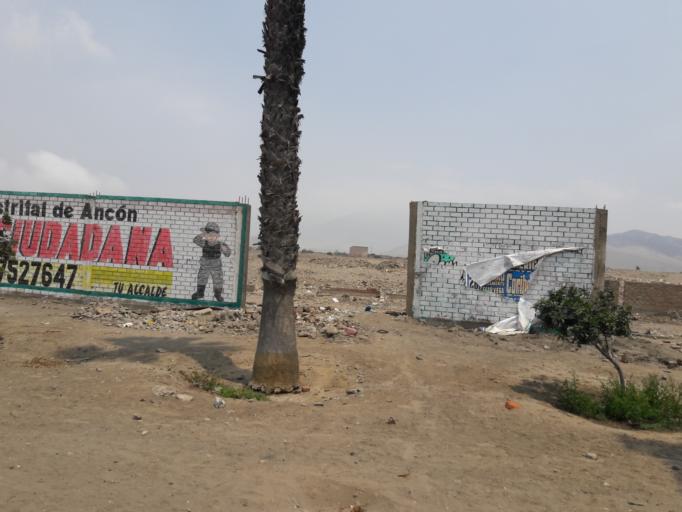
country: PE
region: Lima
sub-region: Lima
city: Santa Rosa
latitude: -11.7707
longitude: -77.1700
